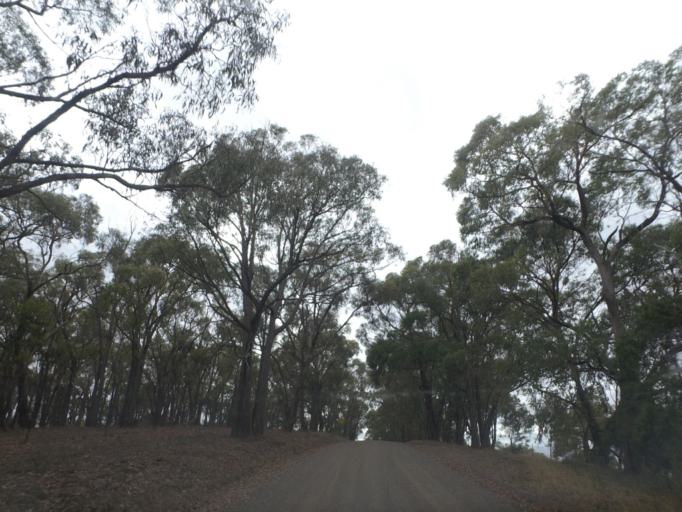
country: AU
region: Victoria
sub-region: Yarra Ranges
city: Yarra Glen
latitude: -37.6622
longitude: 145.3359
